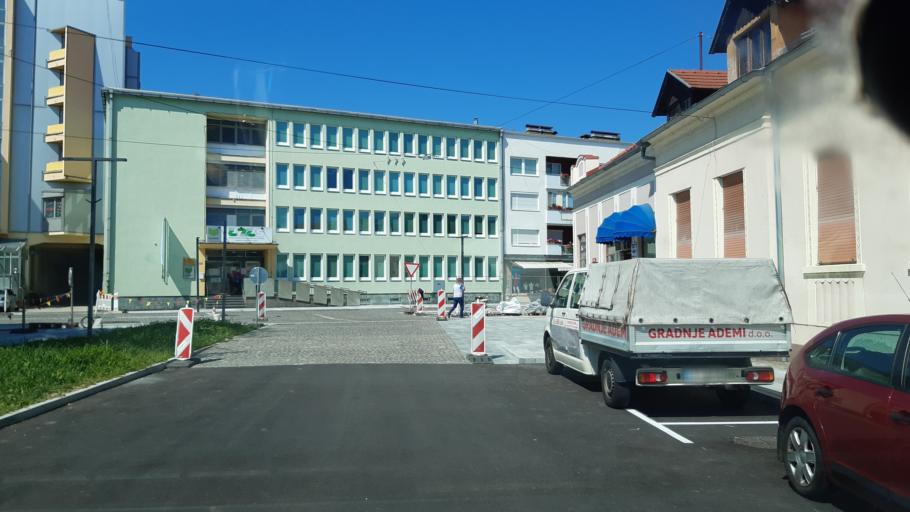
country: SI
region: Murska Sobota
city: Murska Sobota
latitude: 46.6590
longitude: 16.1669
